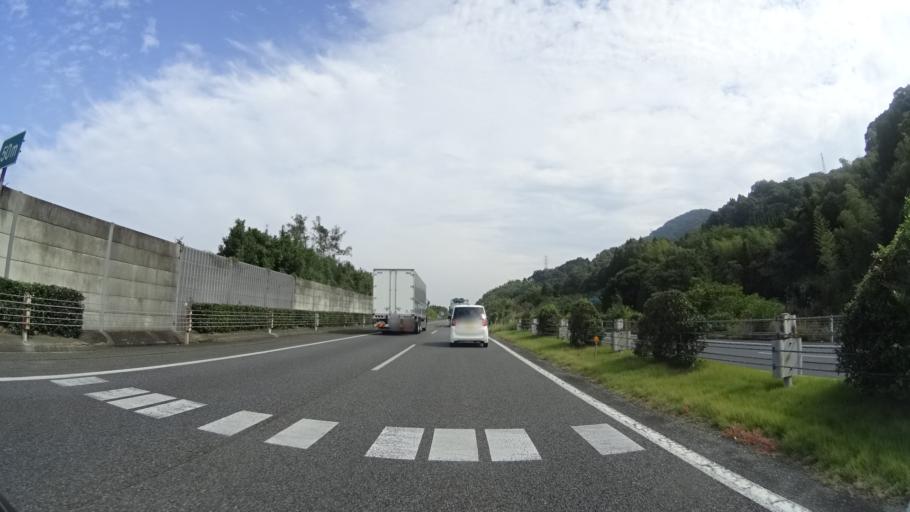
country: JP
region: Kumamoto
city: Yatsushiro
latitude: 32.5270
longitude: 130.6643
